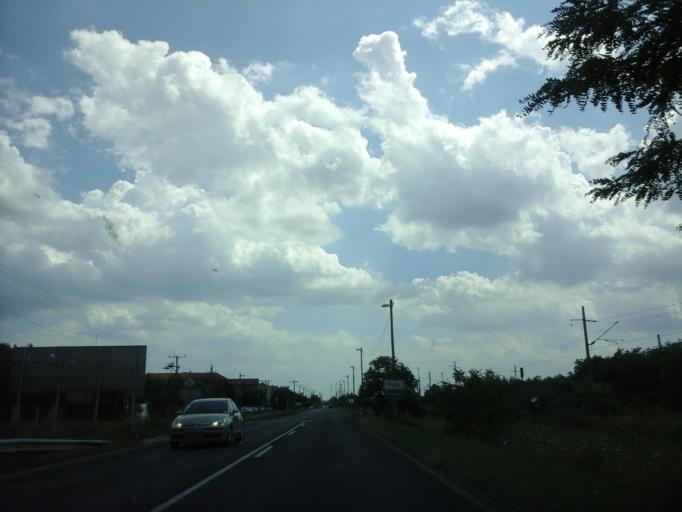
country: HU
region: Gyor-Moson-Sopron
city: Rajka
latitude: 48.0039
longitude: 17.1866
